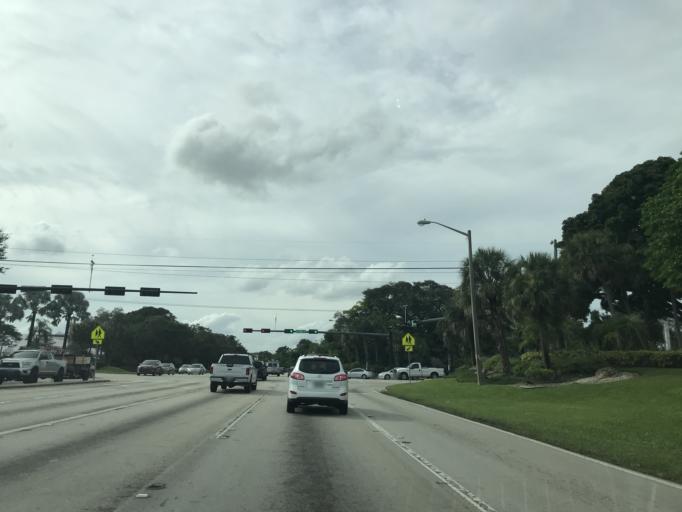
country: US
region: Florida
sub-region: Broward County
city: Coconut Creek
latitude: 26.2598
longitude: -80.1857
